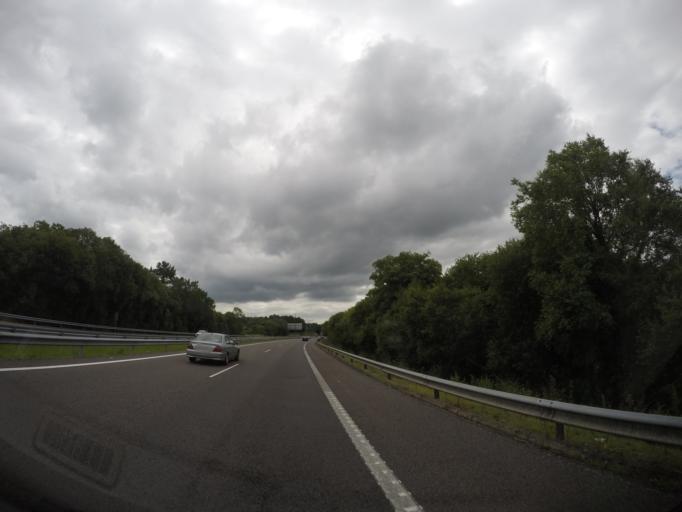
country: ES
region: Galicia
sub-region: Provincia da Coruna
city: Betanzos
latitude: 43.2702
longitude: -8.2537
